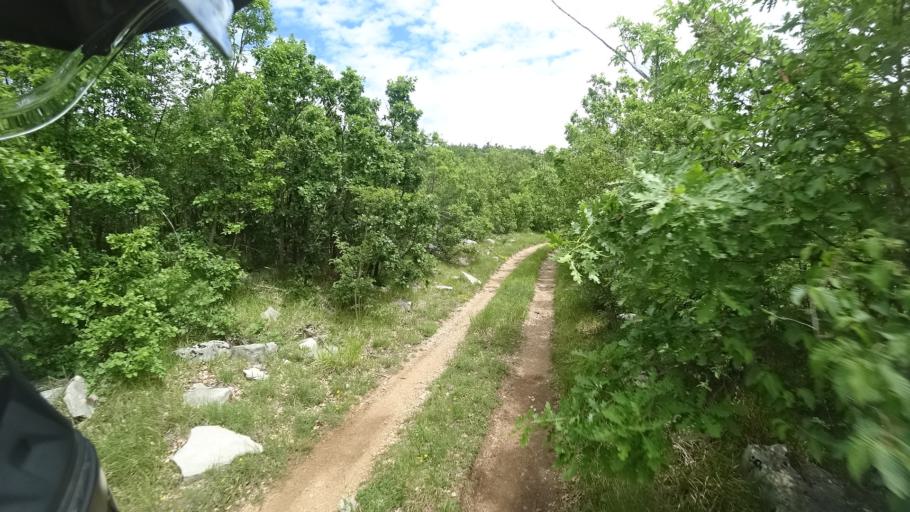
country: HR
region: Splitsko-Dalmatinska
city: Hrvace
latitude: 43.8848
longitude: 16.5831
